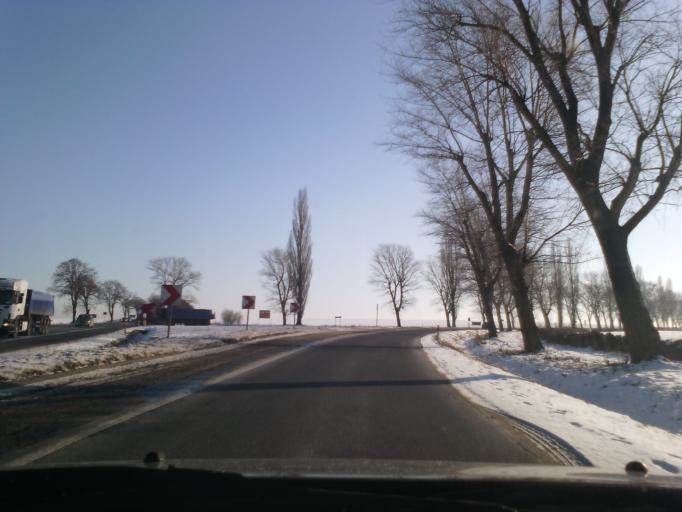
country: PL
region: Lower Silesian Voivodeship
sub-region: Powiat swidnicki
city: Stanowice
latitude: 50.9224
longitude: 16.3685
